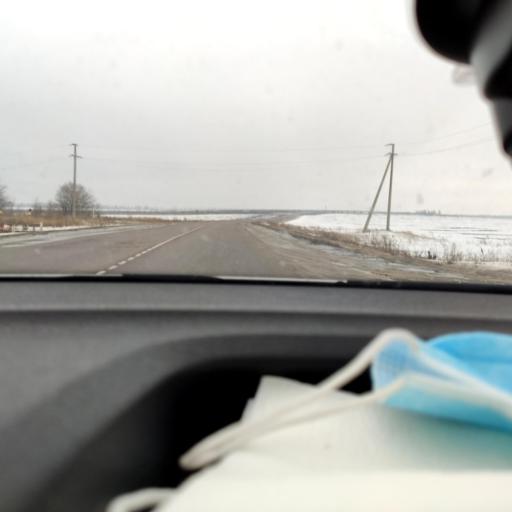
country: RU
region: Voronezj
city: Novaya Usman'
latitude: 51.5909
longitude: 39.3526
